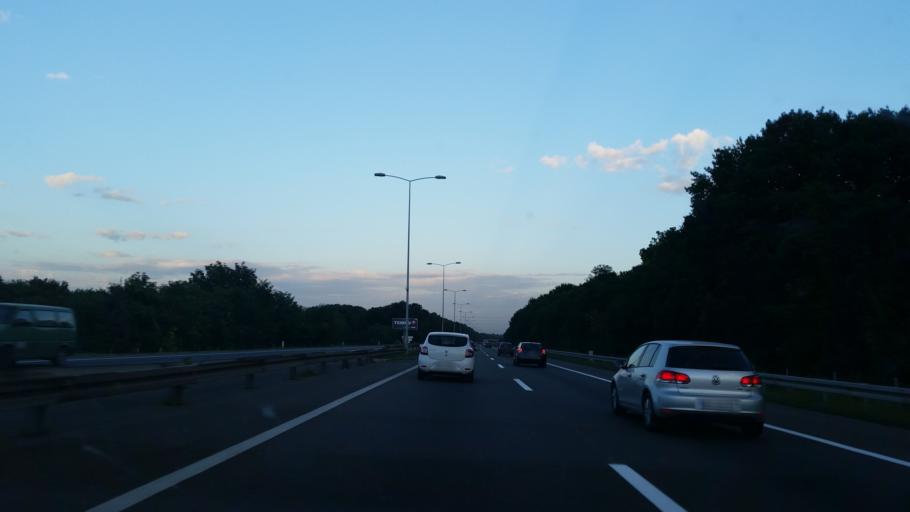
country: RS
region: Central Serbia
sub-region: Belgrade
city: Surcin
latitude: 44.8344
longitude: 20.3306
